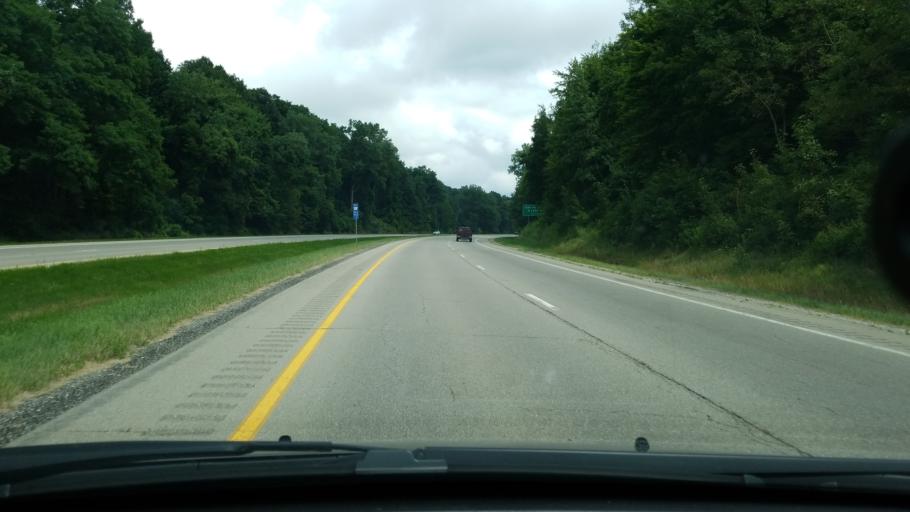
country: US
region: Ohio
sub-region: Lorain County
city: Amherst
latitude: 41.4083
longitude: -82.2533
